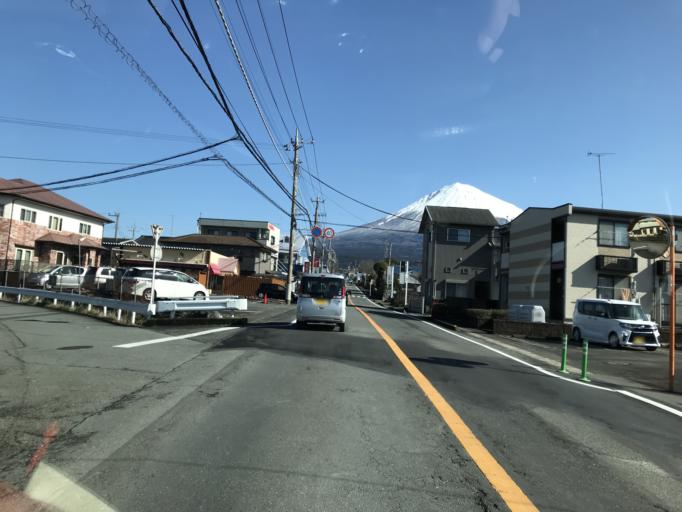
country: JP
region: Shizuoka
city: Fujinomiya
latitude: 35.2492
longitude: 138.6270
